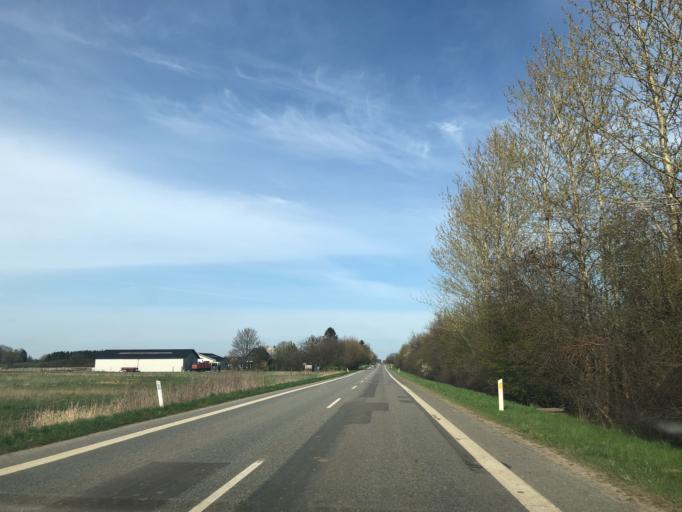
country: DK
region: Zealand
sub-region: Faxe Kommune
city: Ronnede
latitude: 55.2903
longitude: 12.0391
